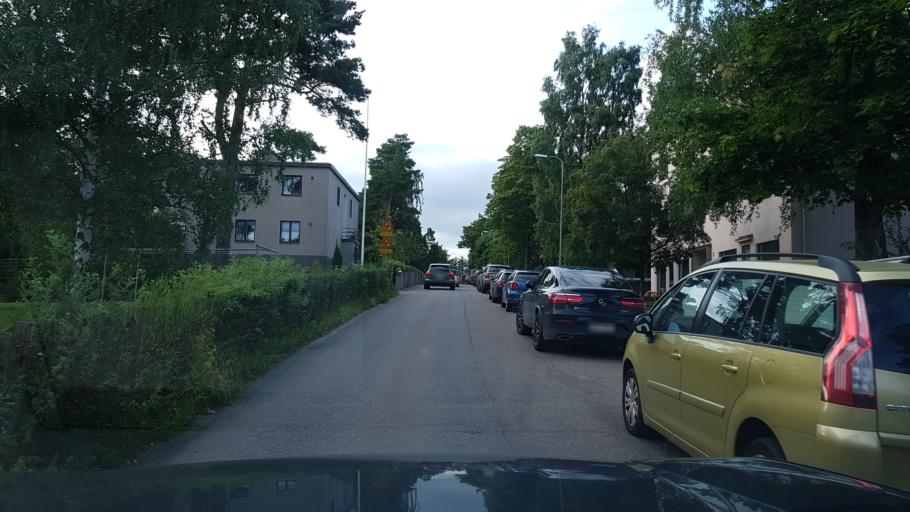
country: FI
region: Uusimaa
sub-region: Helsinki
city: Teekkarikylae
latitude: 60.1959
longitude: 24.8726
